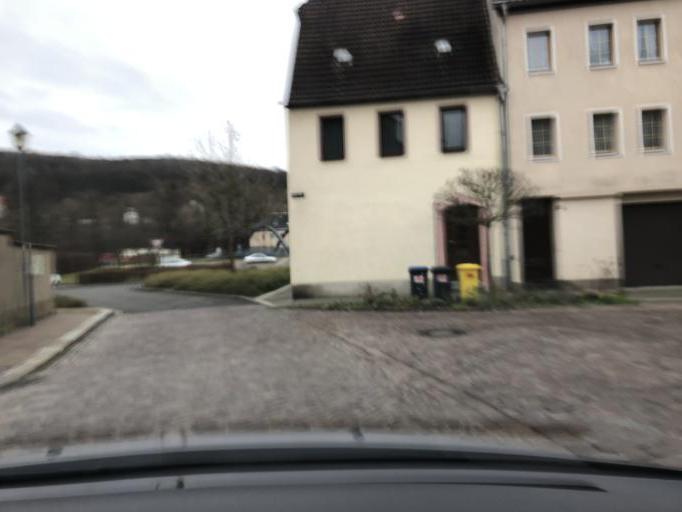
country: DE
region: Saxony
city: Rosswein
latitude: 51.0640
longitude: 13.1855
